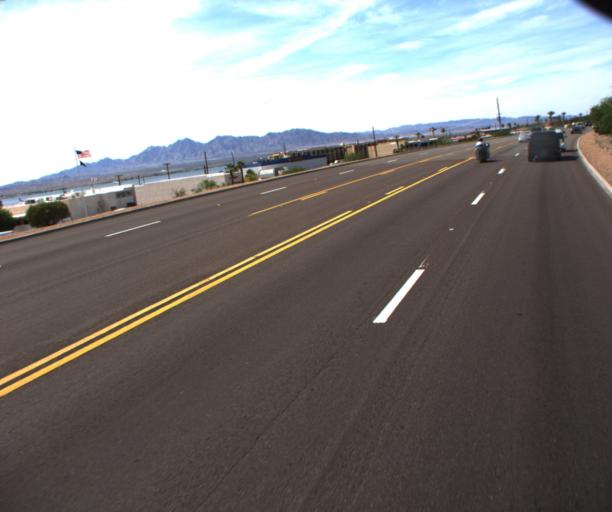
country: US
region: Arizona
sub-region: Mohave County
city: Lake Havasu City
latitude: 34.4759
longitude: -114.3477
